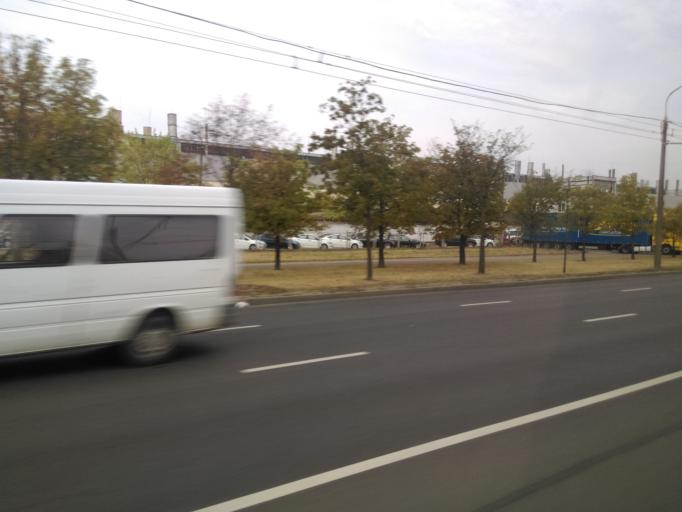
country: BY
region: Minsk
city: Minsk
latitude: 53.8973
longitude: 27.6414
